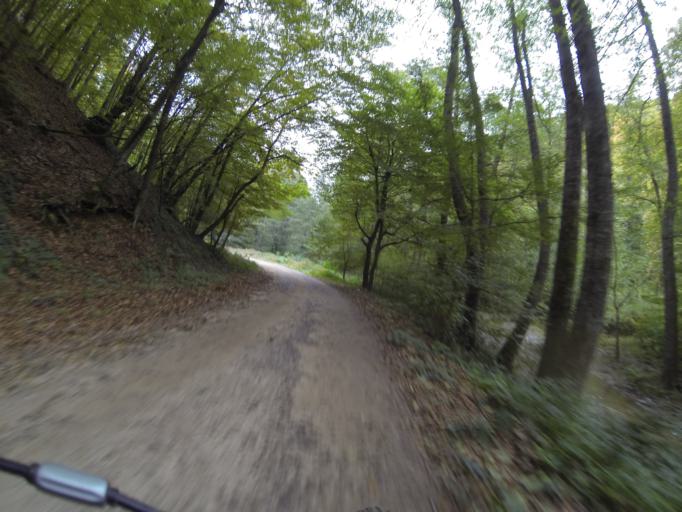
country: RO
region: Gorj
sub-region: Comuna Tismana
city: Pocruia
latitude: 45.0545
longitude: 22.9078
